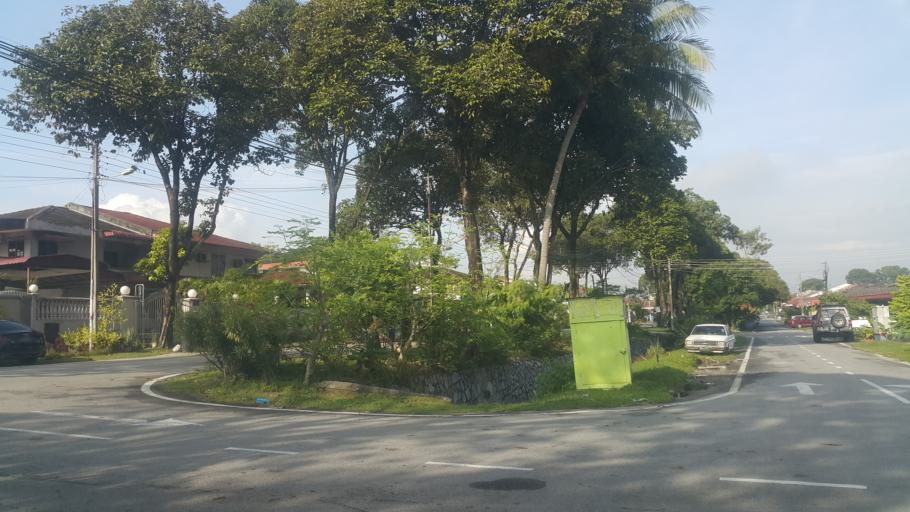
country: MY
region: Selangor
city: Klang
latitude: 3.0123
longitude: 101.4456
